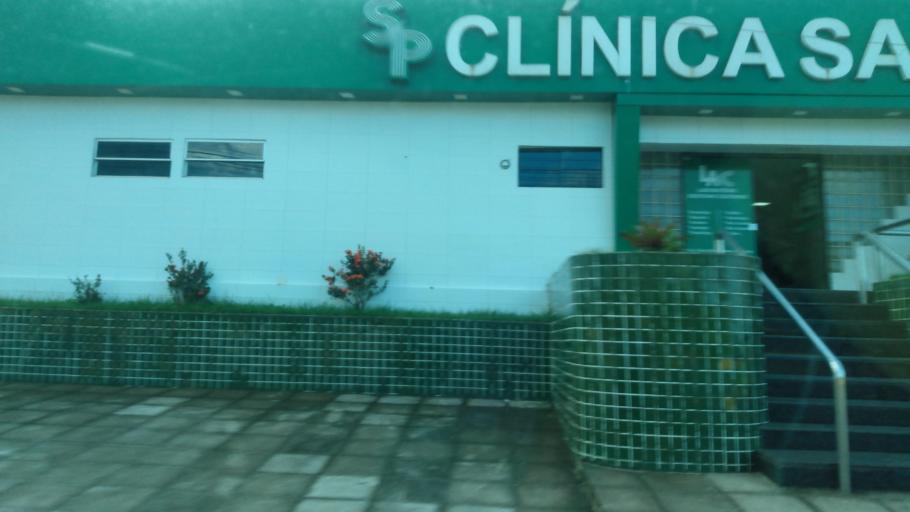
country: BR
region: Pernambuco
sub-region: Palmares
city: Palmares
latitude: -8.6801
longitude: -35.5810
